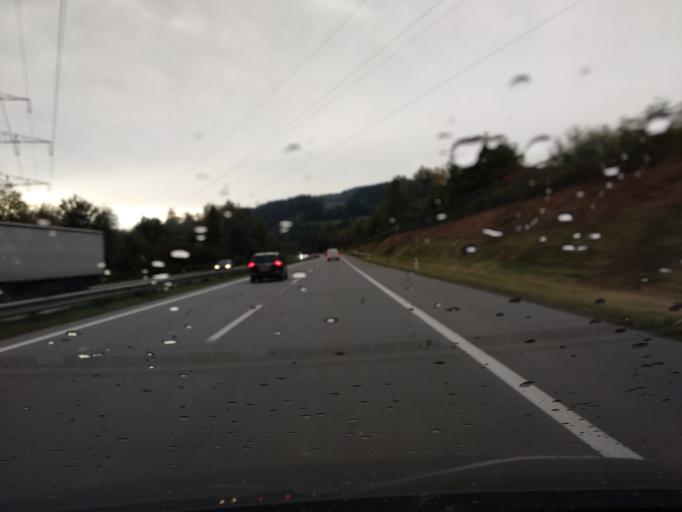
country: AT
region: Vorarlberg
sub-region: Politischer Bezirk Feldkirch
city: Satteins
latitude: 47.2172
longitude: 9.6573
